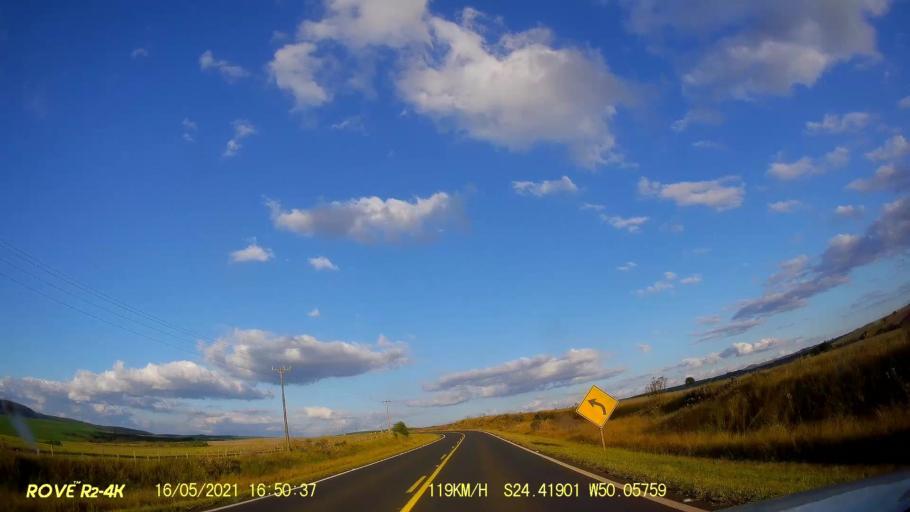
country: BR
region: Parana
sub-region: Pirai Do Sul
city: Pirai do Sul
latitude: -24.4195
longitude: -50.0572
